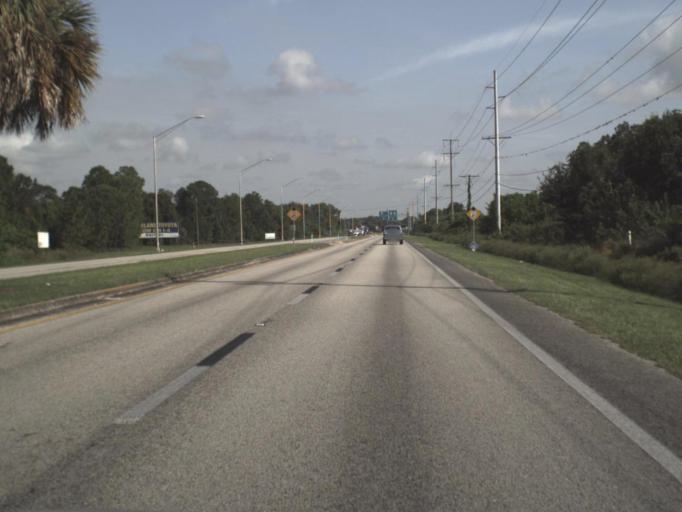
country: US
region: Florida
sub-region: Polk County
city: Lake Alfred
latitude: 28.0685
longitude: -81.7326
